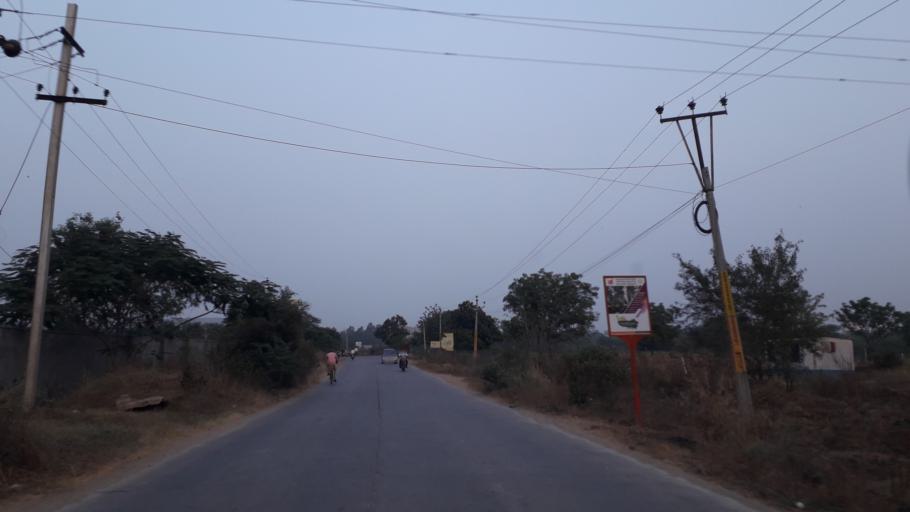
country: IN
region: Telangana
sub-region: Medak
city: Patancheru
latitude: 17.5202
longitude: 78.2400
